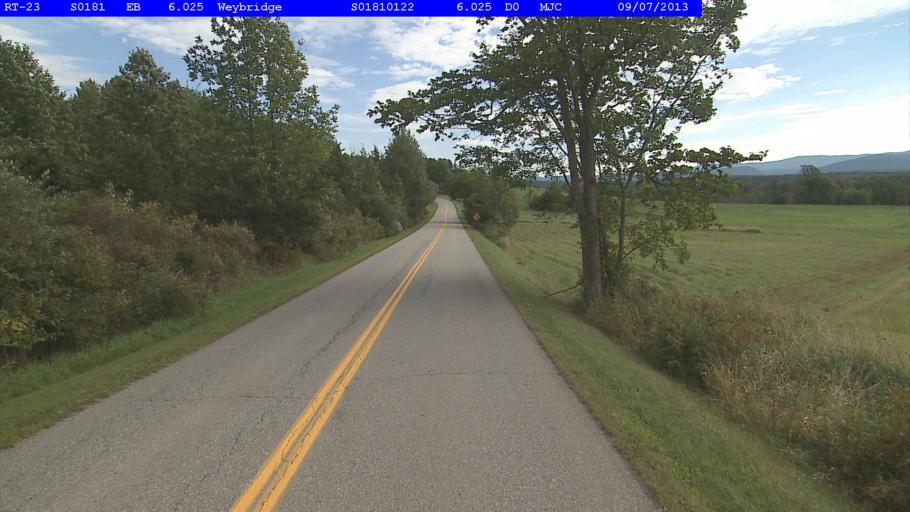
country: US
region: Vermont
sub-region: Addison County
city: Vergennes
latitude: 44.0769
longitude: -73.2531
